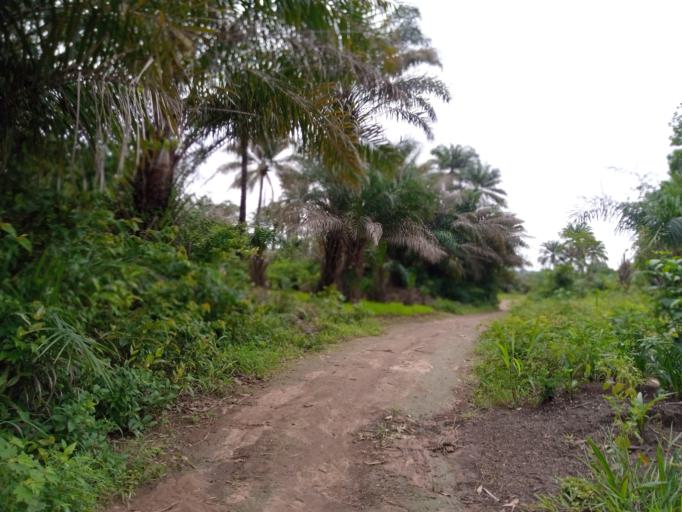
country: SL
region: Northern Province
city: Masoyila
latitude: 8.5808
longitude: -13.1880
